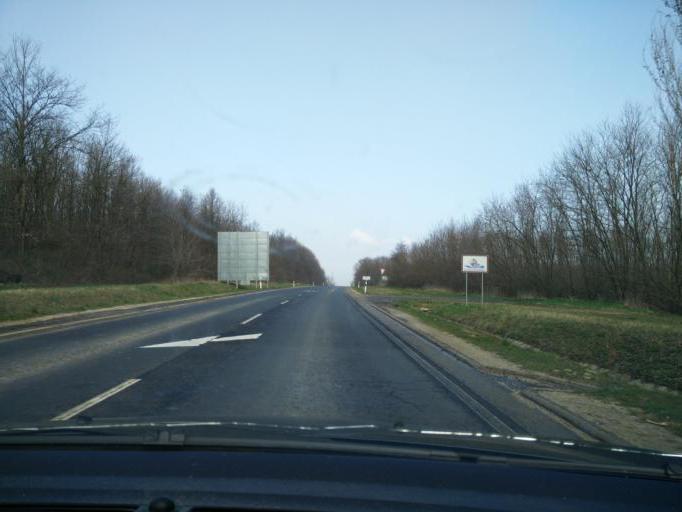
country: HU
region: Somogy
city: Balatonbereny
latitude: 46.6729
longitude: 17.3457
